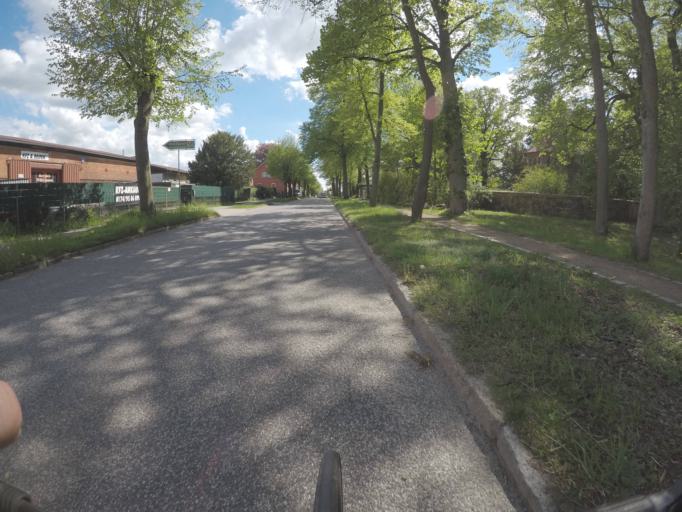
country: DE
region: Brandenburg
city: Bernau bei Berlin
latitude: 52.7024
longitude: 13.5882
